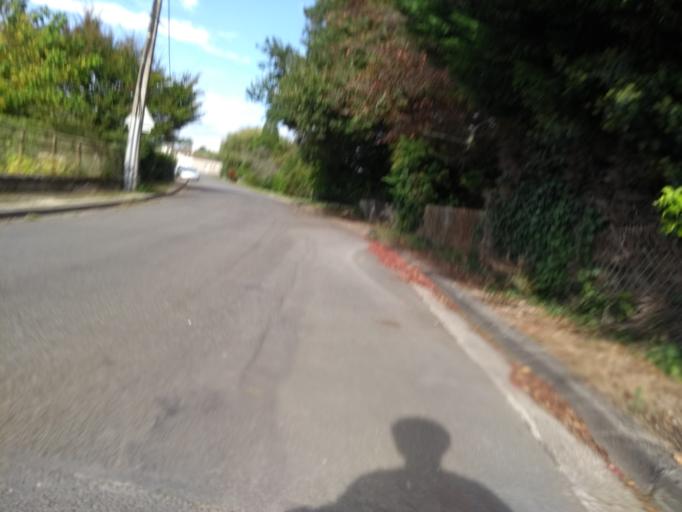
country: FR
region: Aquitaine
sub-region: Departement de la Gironde
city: Gradignan
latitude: 44.7775
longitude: -0.6214
